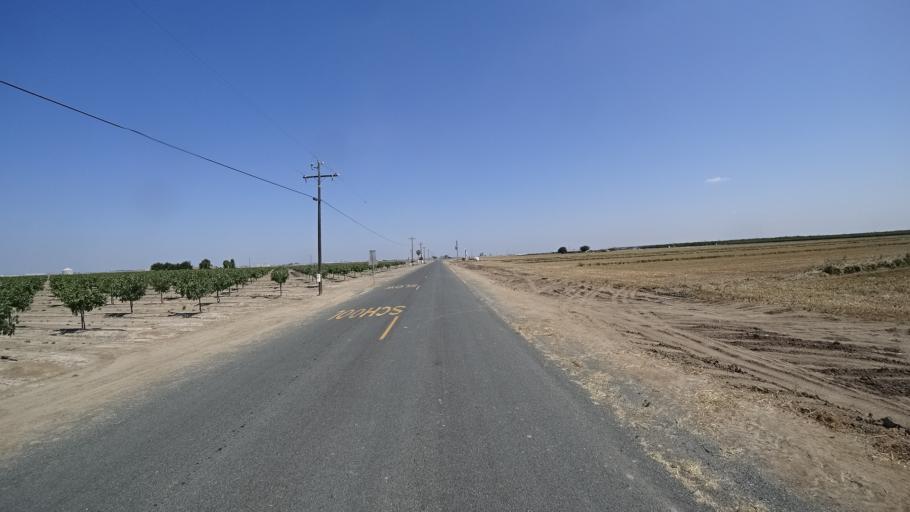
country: US
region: California
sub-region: Kings County
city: Home Garden
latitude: 36.2424
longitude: -119.6189
